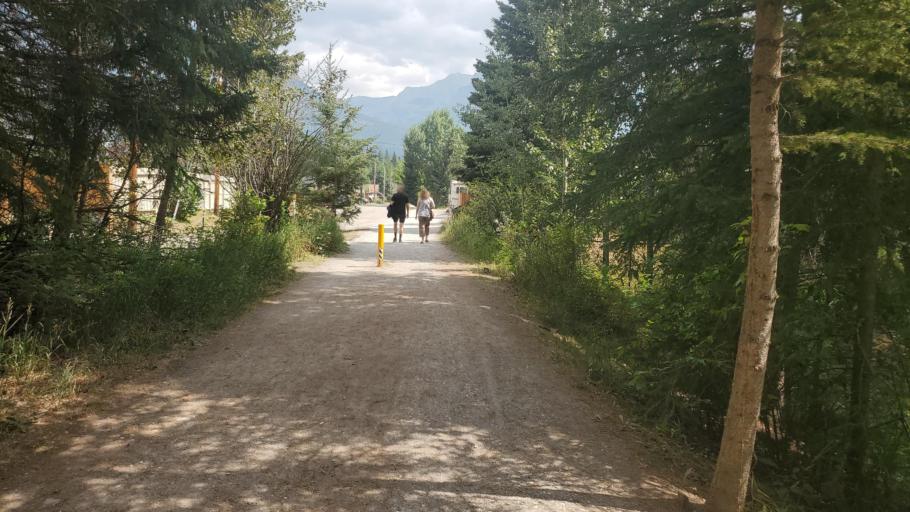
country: CA
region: Alberta
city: Canmore
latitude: 51.0918
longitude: -115.3677
